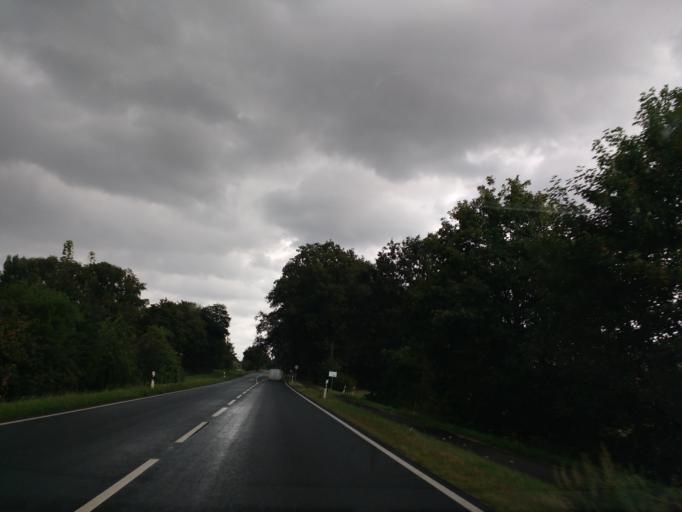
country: DE
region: Lower Saxony
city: Glandorf
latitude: 52.0882
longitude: 7.9815
